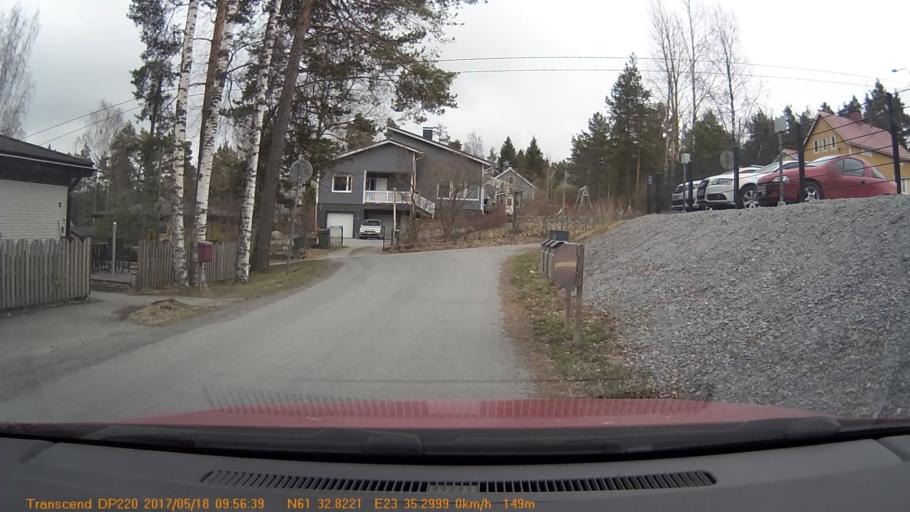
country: FI
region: Pirkanmaa
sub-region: Tampere
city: Yloejaervi
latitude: 61.5470
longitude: 23.5883
